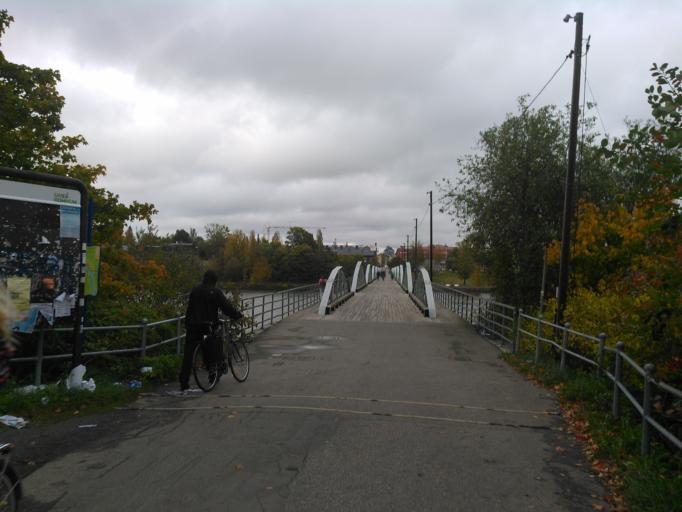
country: SE
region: Vaesterbotten
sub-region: Umea Kommun
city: Umea
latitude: 63.8235
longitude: 20.2482
